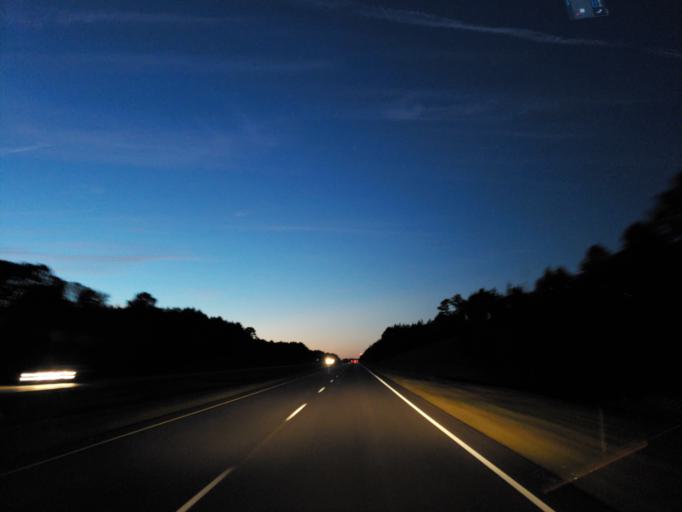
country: US
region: Mississippi
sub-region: Clarke County
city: Quitman
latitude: 32.0786
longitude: -88.6905
